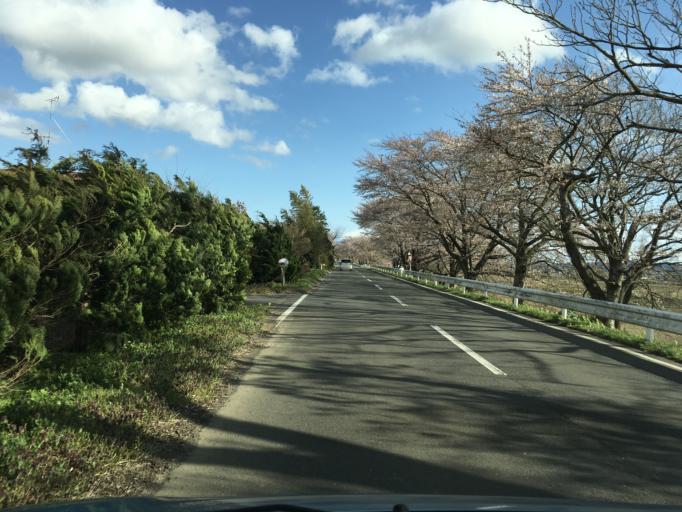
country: JP
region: Miyagi
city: Wakuya
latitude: 38.6488
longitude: 141.1447
